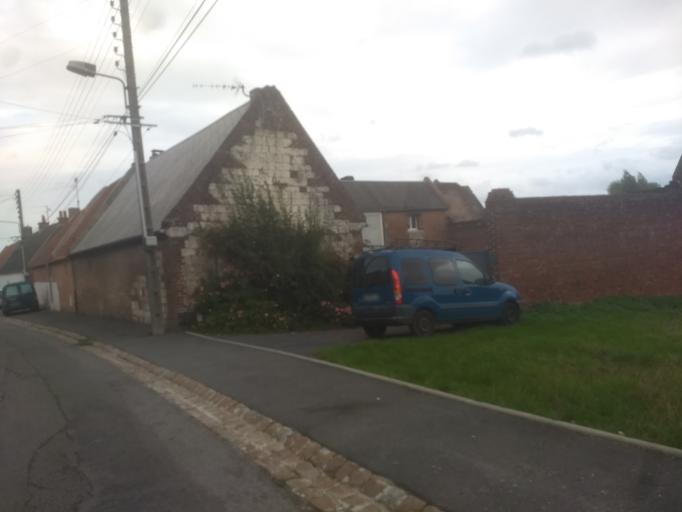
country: FR
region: Nord-Pas-de-Calais
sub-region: Departement du Pas-de-Calais
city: Achicourt
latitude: 50.2732
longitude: 2.7527
